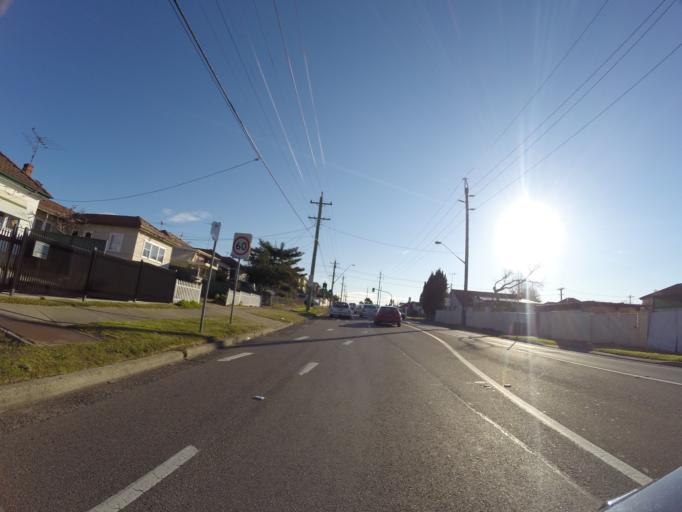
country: AU
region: New South Wales
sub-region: Bankstown
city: Regents Park
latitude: -33.8625
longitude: 151.0021
